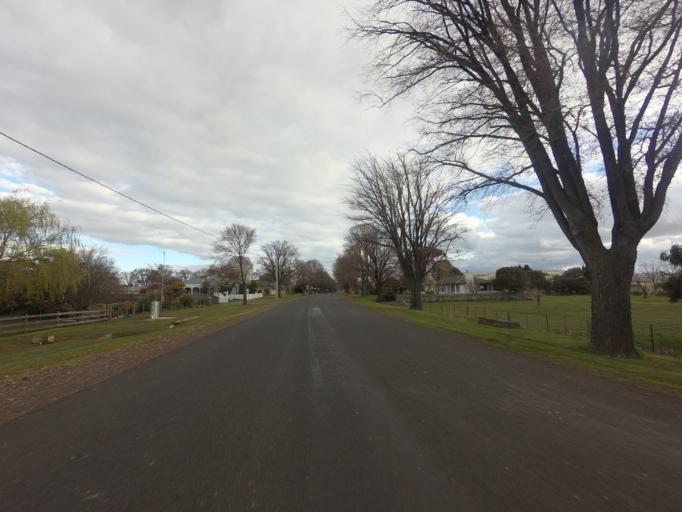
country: AU
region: Tasmania
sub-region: Northern Midlands
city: Evandale
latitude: -42.0257
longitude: 147.4933
